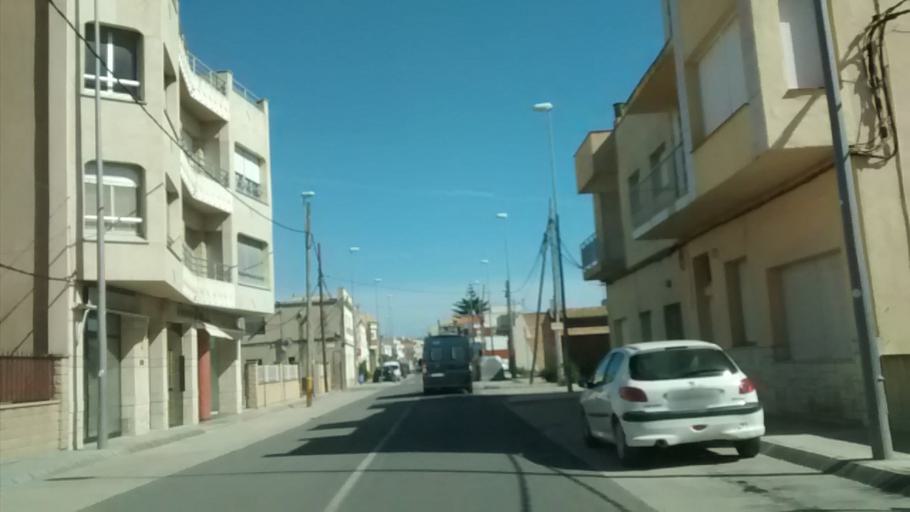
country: ES
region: Catalonia
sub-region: Provincia de Tarragona
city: Deltebre
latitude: 40.7156
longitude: 0.7457
